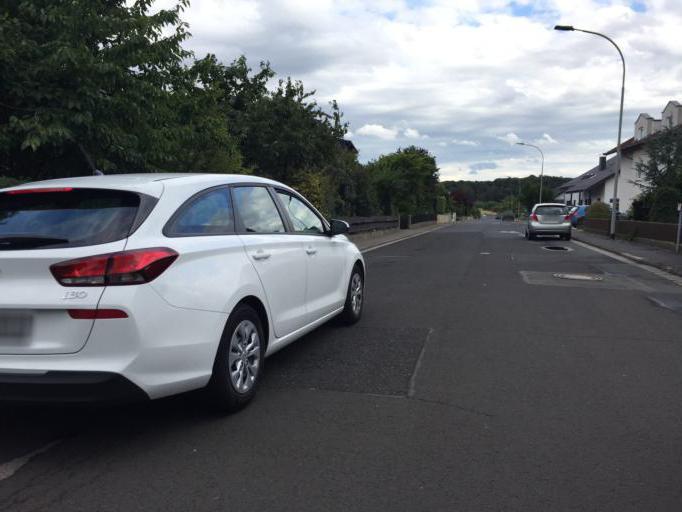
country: DE
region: Hesse
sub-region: Regierungsbezirk Giessen
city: Langgons
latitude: 50.4919
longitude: 8.6720
